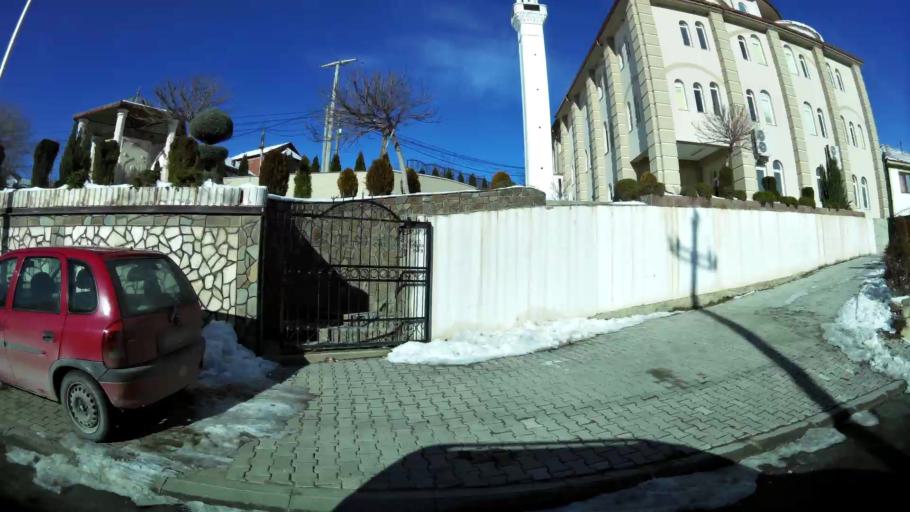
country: MK
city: Ljubin
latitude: 41.9787
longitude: 21.3035
